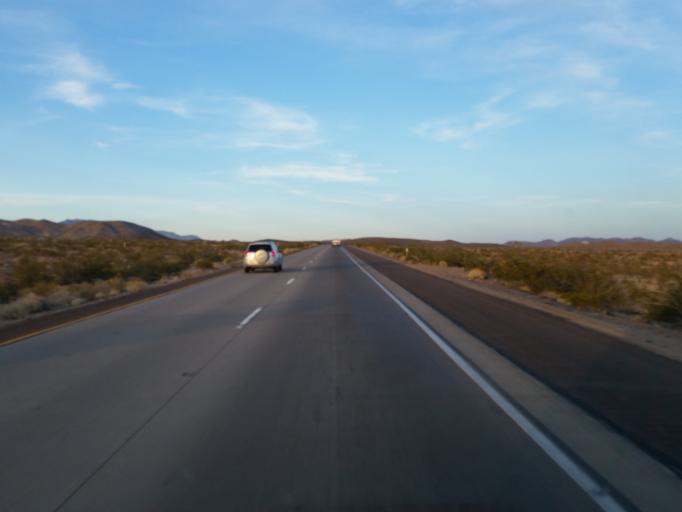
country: US
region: California
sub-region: San Bernardino County
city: Twentynine Palms
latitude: 34.7237
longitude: -115.9462
